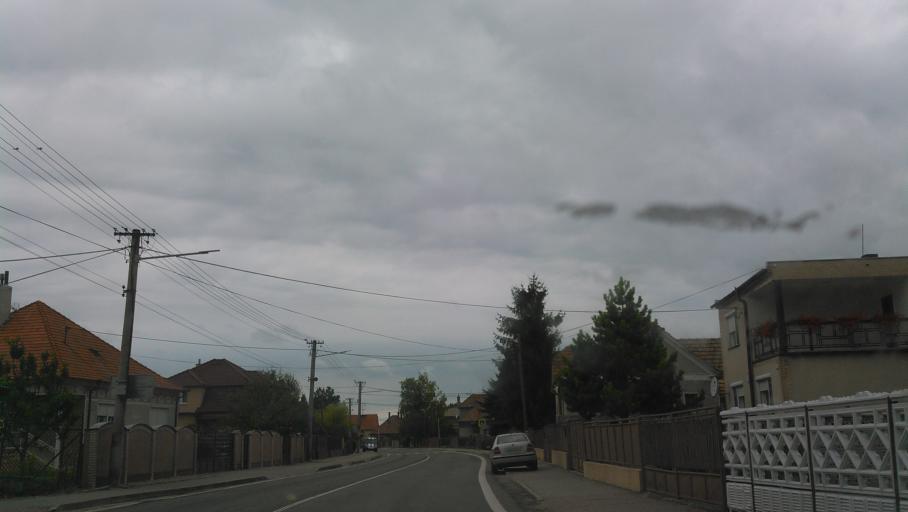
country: SK
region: Trnavsky
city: Dunajska Streda
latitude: 47.9662
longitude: 17.6850
